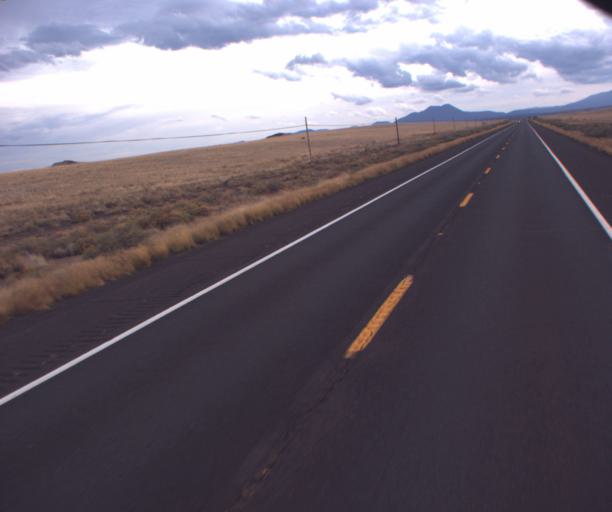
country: US
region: Arizona
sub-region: Coconino County
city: Flagstaff
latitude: 35.6170
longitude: -111.5227
